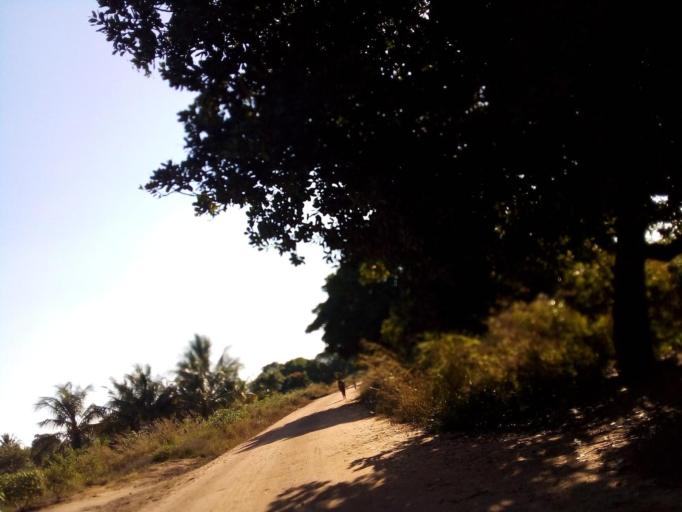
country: MZ
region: Zambezia
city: Quelimane
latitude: -17.5045
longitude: 36.5846
